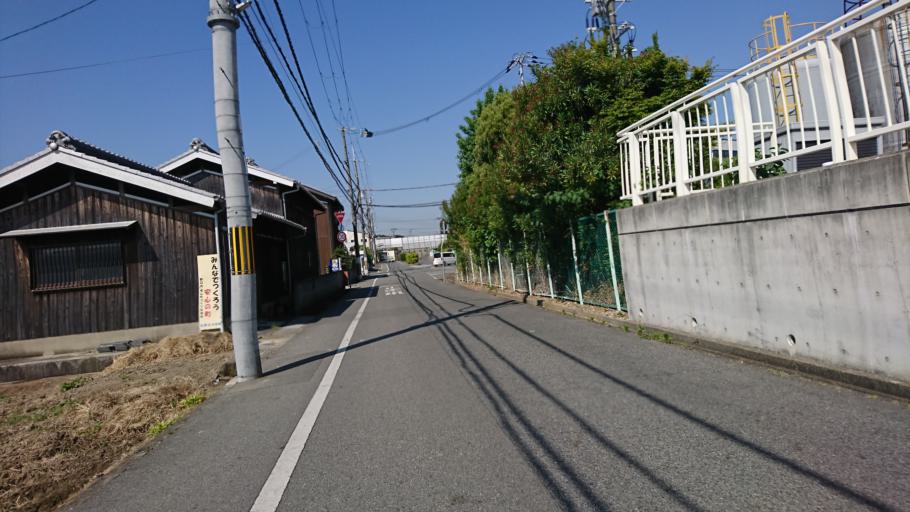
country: JP
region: Hyogo
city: Kakogawacho-honmachi
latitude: 34.7555
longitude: 134.8647
